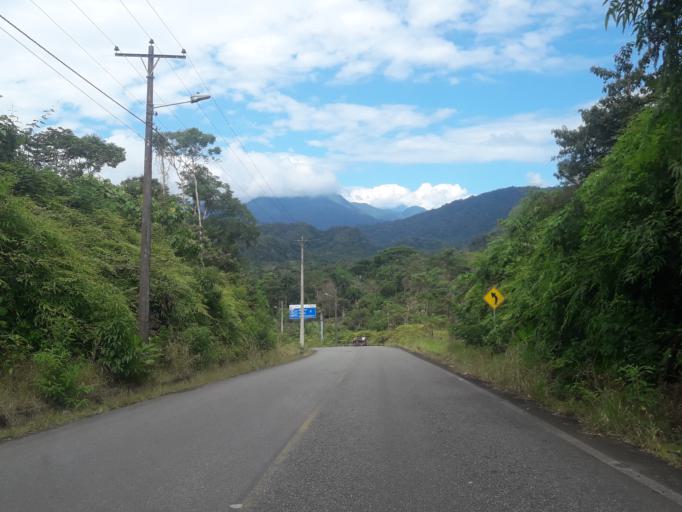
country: EC
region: Napo
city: Tena
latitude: -1.0595
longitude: -77.8995
